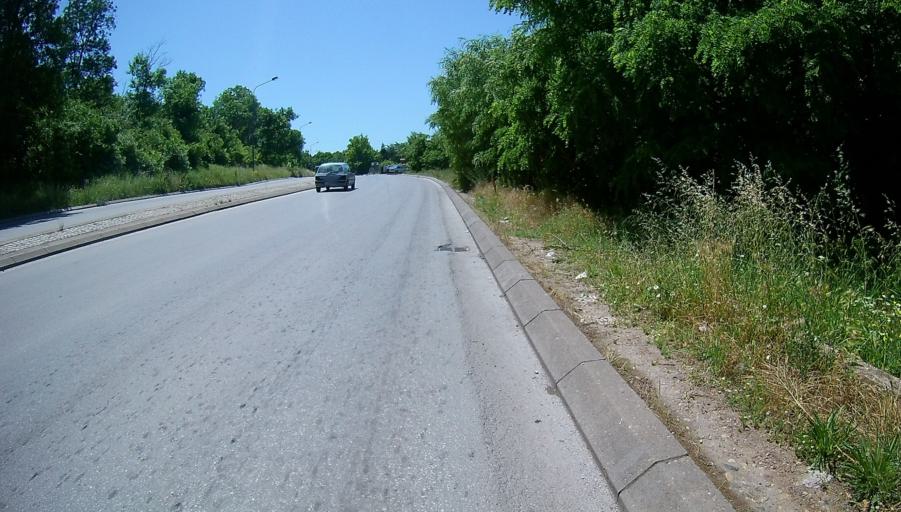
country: RS
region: Central Serbia
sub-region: Nisavski Okrug
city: Nis
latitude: 43.3098
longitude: 21.8712
